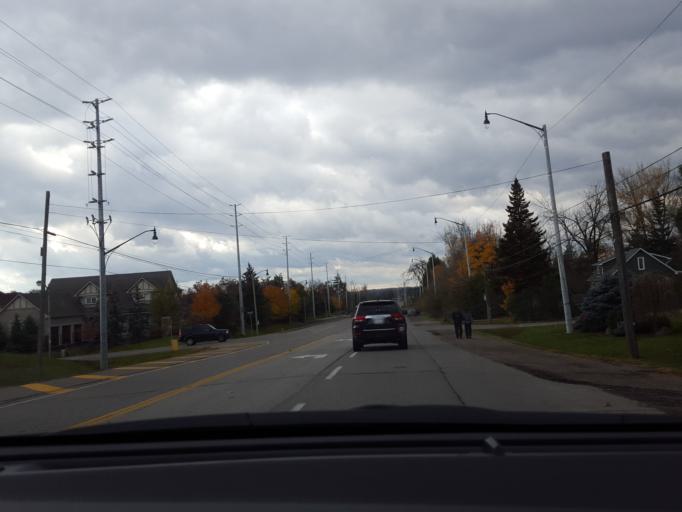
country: CA
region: Ontario
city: Brampton
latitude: 43.6544
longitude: -79.7948
